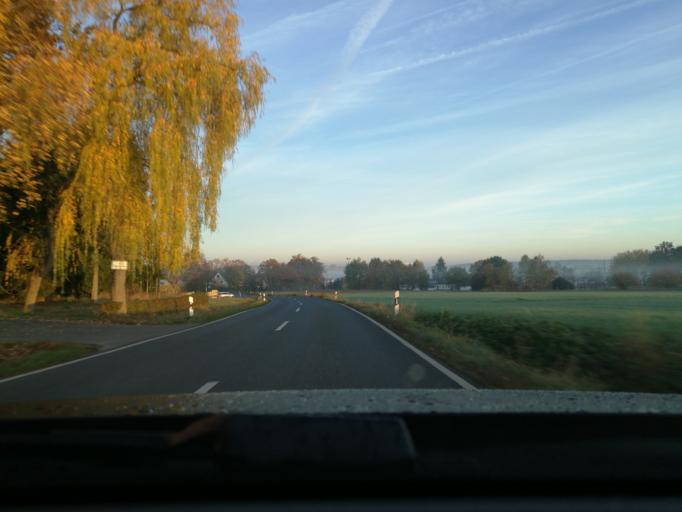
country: DE
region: Bavaria
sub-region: Regierungsbezirk Mittelfranken
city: Obermichelbach
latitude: 49.5540
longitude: 10.9221
